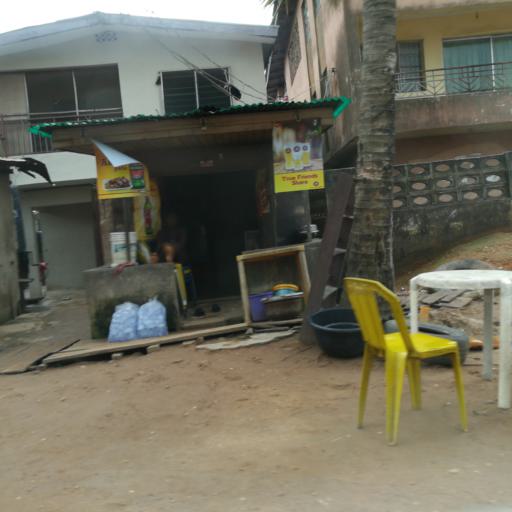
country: NG
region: Lagos
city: Agege
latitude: 6.6050
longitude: 3.2965
